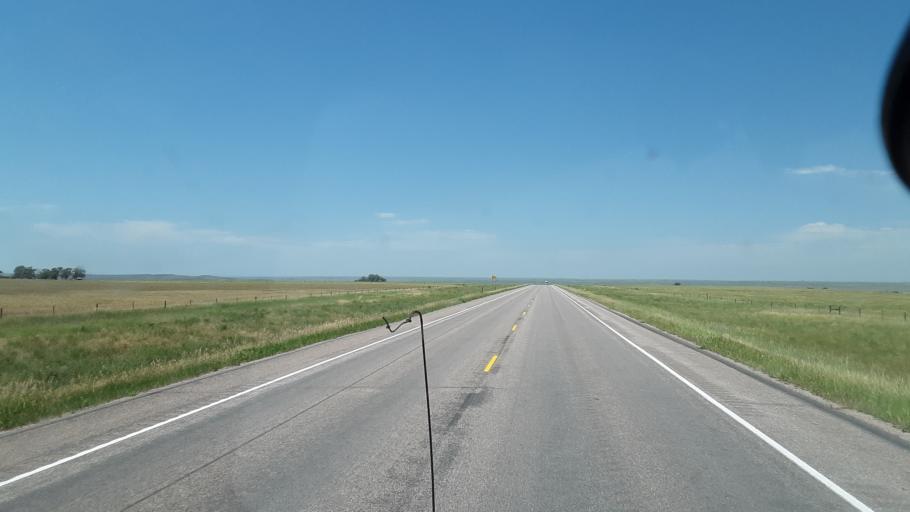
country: US
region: South Dakota
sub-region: Pennington County
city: Box Elder
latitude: 43.8662
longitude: -102.6194
